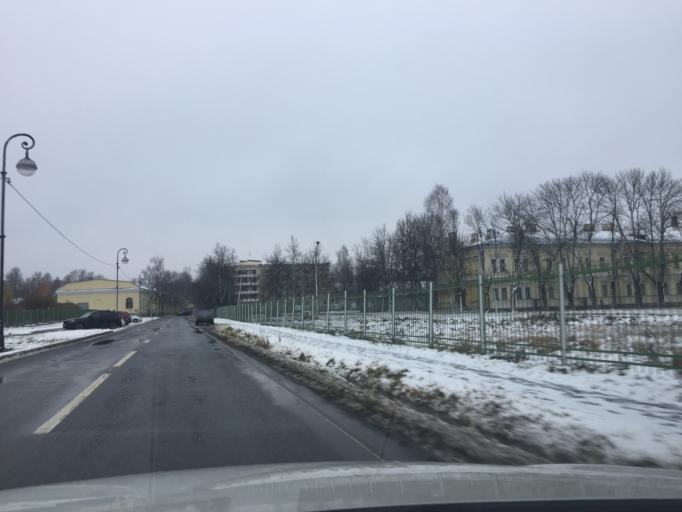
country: RU
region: St.-Petersburg
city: Pushkin
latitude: 59.7050
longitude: 30.3961
